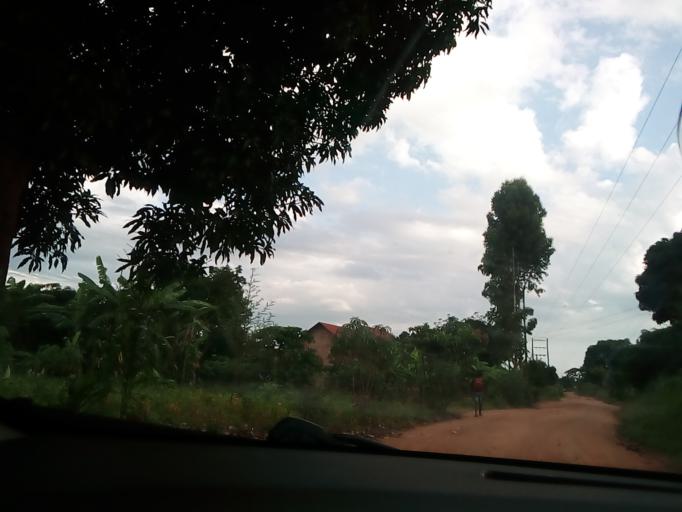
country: UG
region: Central Region
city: Masaka
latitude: -0.3367
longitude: 31.6898
